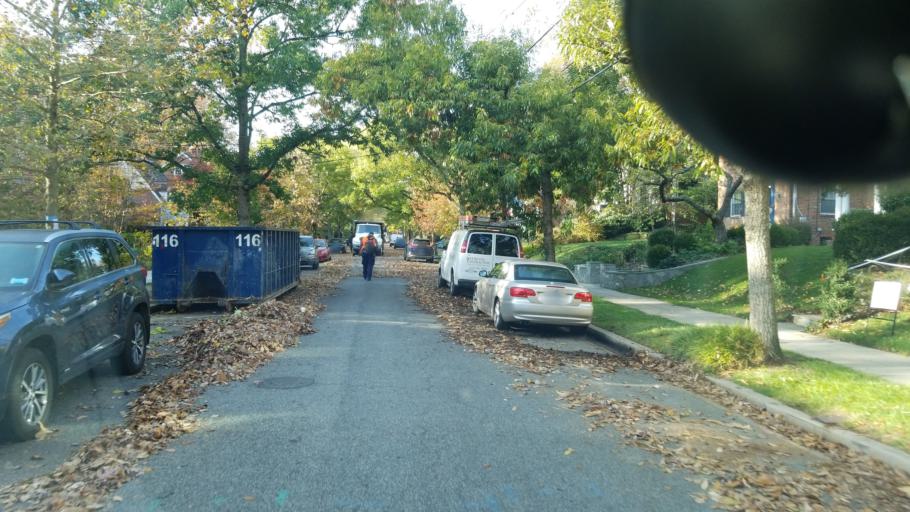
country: US
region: Maryland
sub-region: Montgomery County
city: Chevy Chase
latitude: 38.9749
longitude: -77.0573
